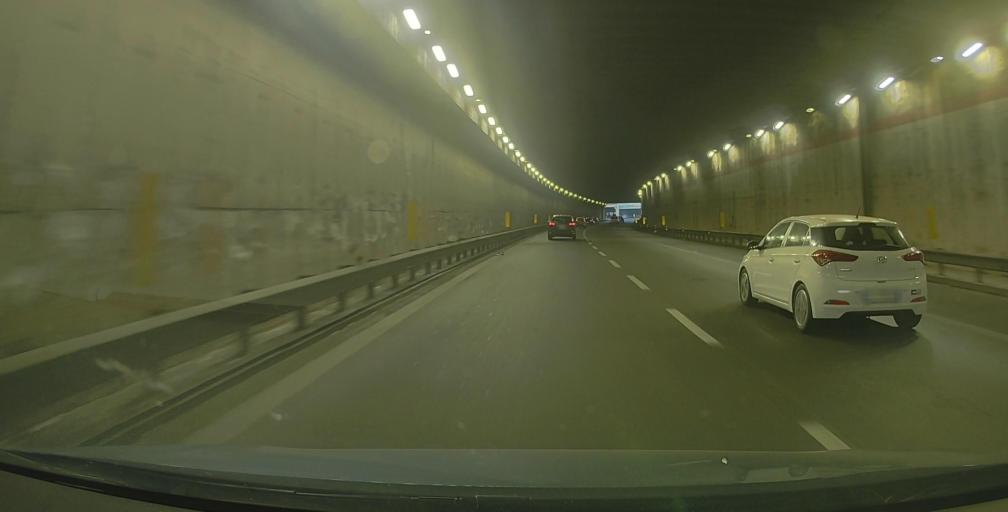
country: IT
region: Sicily
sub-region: Catania
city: Sant'Agata Li Battiati
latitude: 37.5500
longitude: 15.0746
